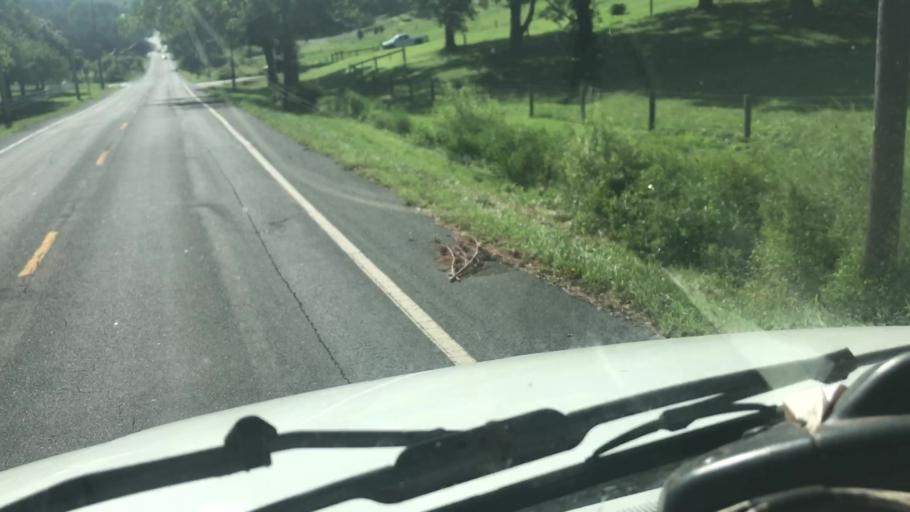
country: US
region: Maryland
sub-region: Carroll County
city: Sykesville
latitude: 39.3046
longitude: -76.9605
